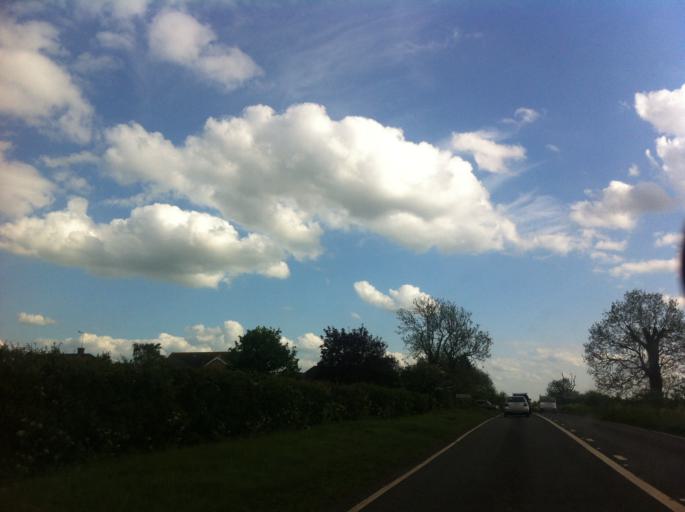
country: GB
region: England
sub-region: Northamptonshire
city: Irchester
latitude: 52.2635
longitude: -0.6778
